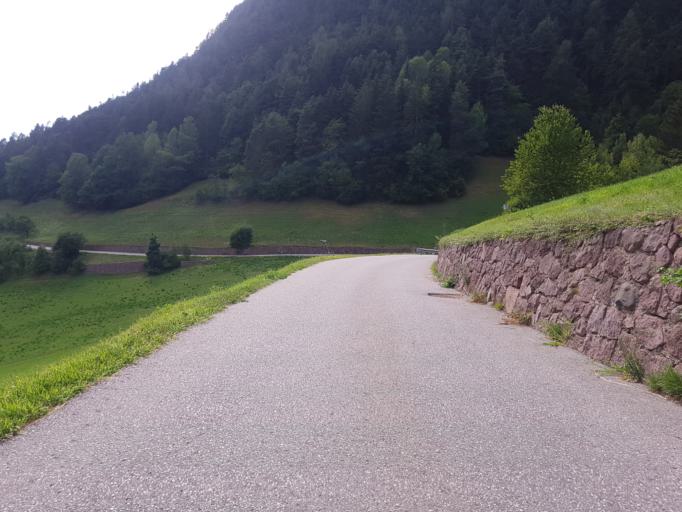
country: IT
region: Trentino-Alto Adige
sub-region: Bolzano
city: Siusi
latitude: 46.5464
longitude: 11.5522
